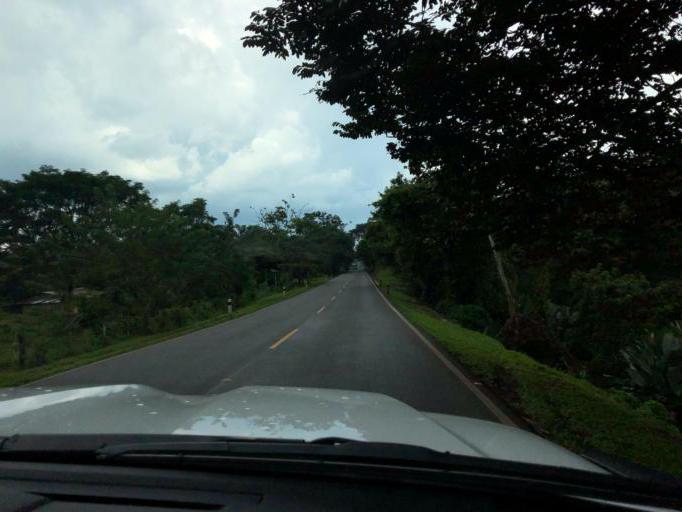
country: NI
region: Chontales
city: Villa Sandino
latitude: 11.9961
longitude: -84.7887
